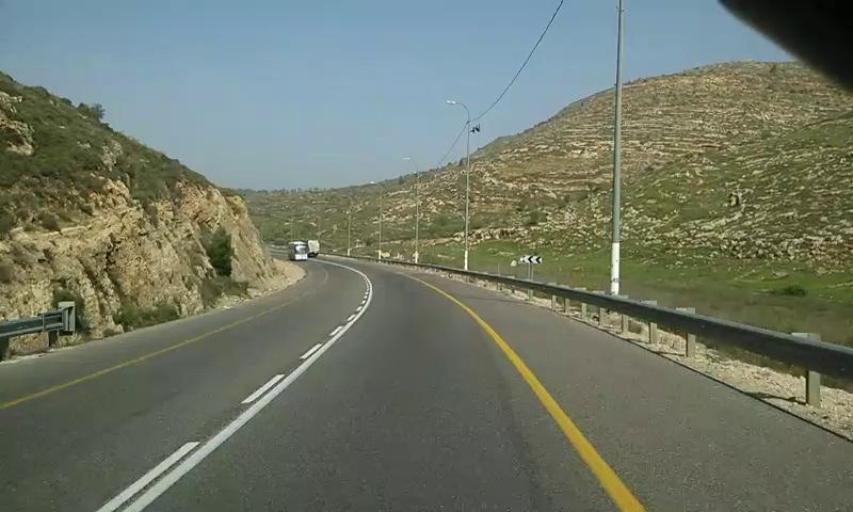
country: PS
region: West Bank
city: Qaryut
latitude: 32.0606
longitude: 35.2809
